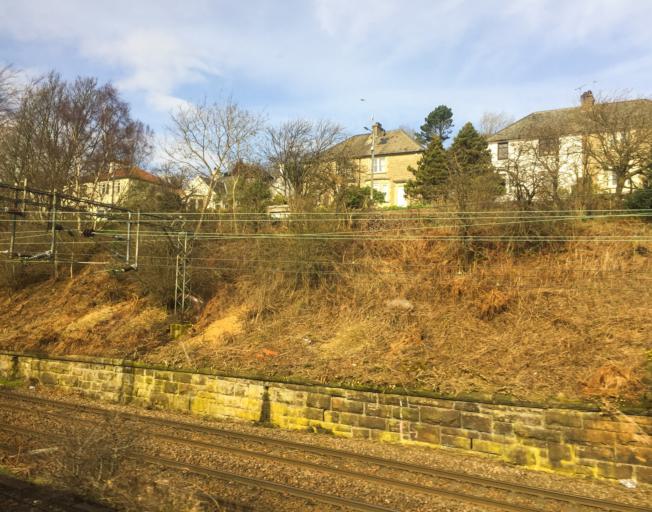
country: GB
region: Scotland
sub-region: East Dunbartonshire
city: Bearsden
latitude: 55.9008
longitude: -4.3273
